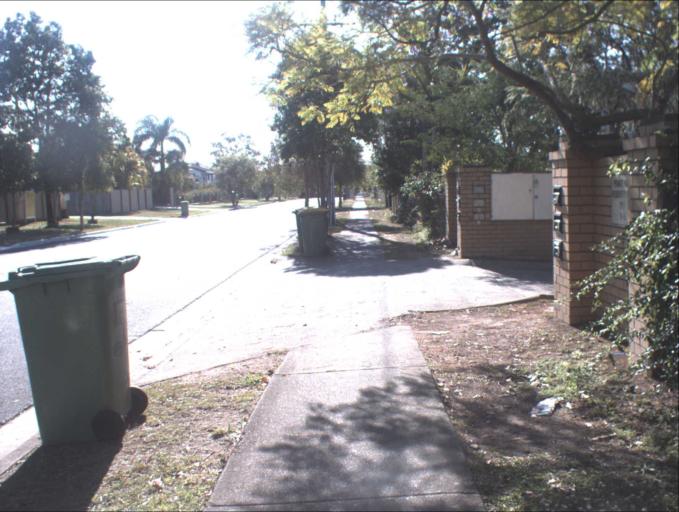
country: AU
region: Queensland
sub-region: Logan
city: Logan City
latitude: -27.6545
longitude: 153.1016
